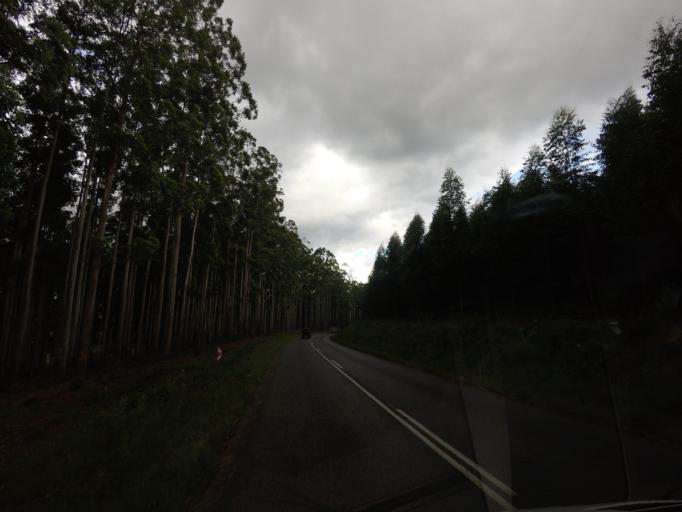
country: ZA
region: Mpumalanga
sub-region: Ehlanzeni District
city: Graksop
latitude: -24.9559
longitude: 30.8999
